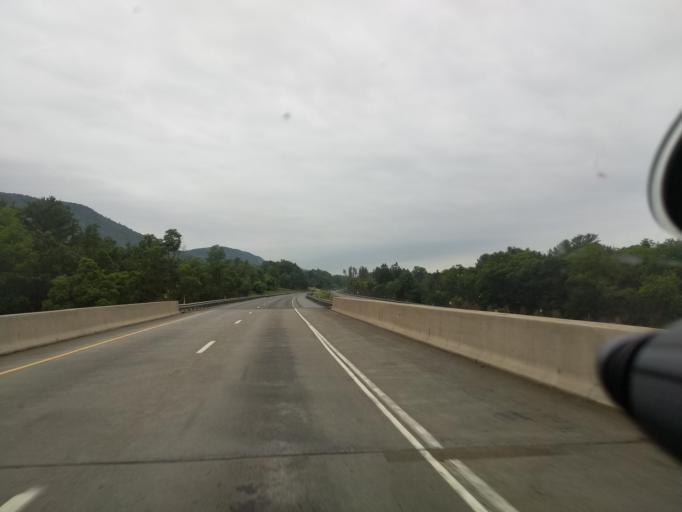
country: US
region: Pennsylvania
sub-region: Clinton County
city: Castanea
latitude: 41.0552
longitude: -77.4370
